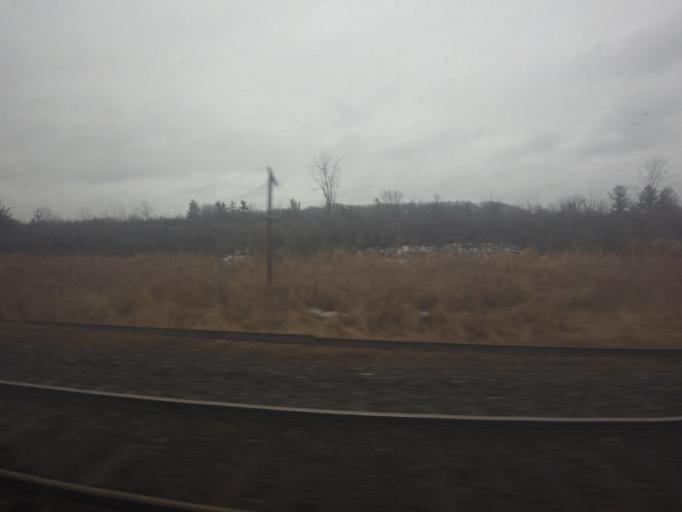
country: CA
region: Ontario
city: Kingston
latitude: 44.2839
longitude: -76.4643
